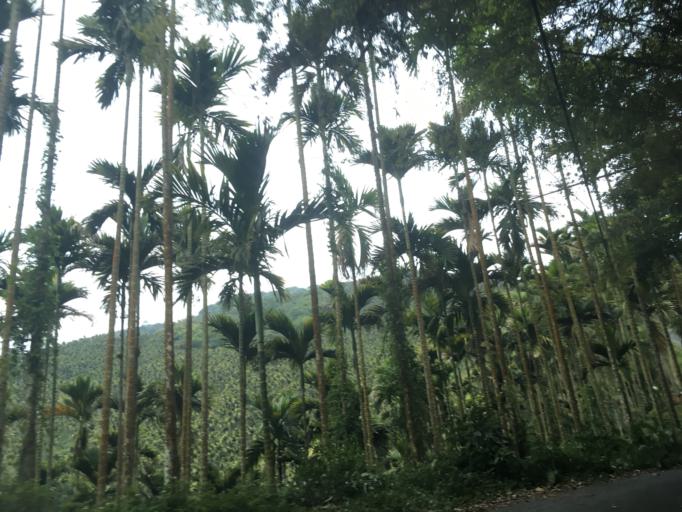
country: TW
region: Taiwan
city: Zhongxing New Village
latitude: 23.9707
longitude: 120.8236
